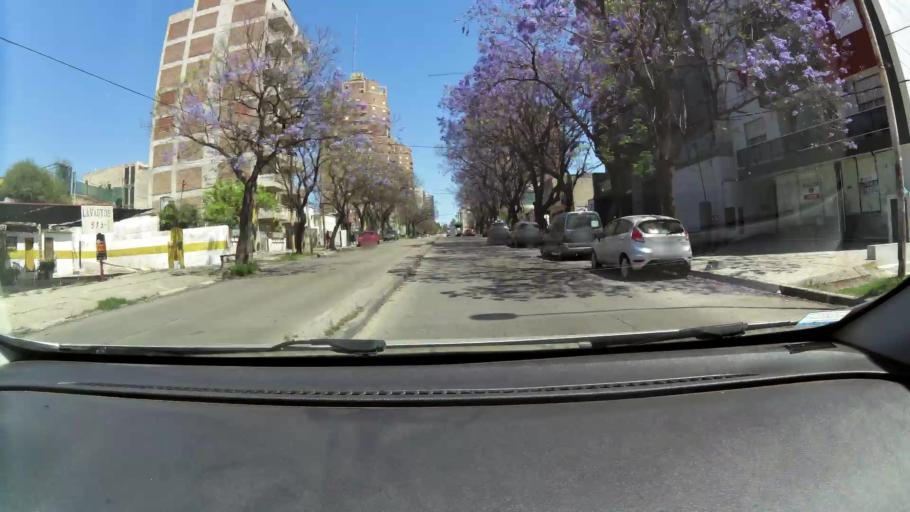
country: AR
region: Cordoba
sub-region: Departamento de Capital
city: Cordoba
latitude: -31.4252
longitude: -64.1958
